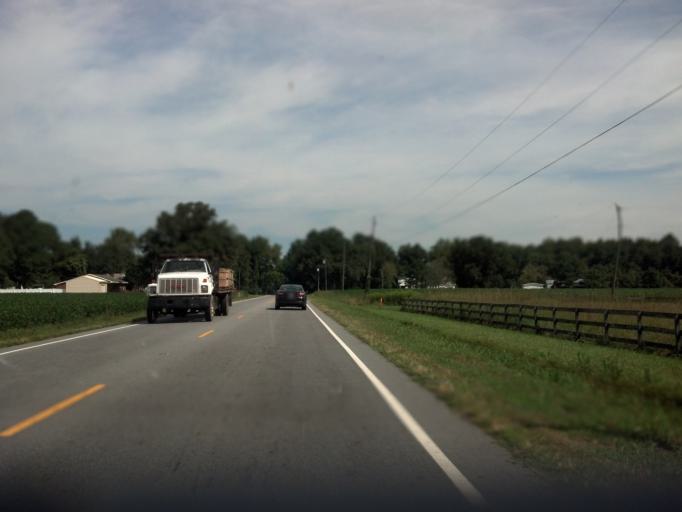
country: US
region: North Carolina
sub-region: Greene County
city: Maury
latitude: 35.5117
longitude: -77.6173
